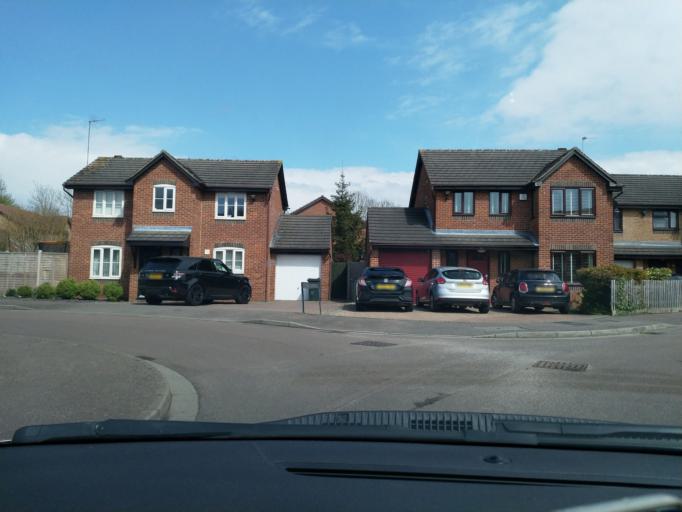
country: GB
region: England
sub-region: Suffolk
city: Woodbridge
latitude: 52.0703
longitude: 1.3192
